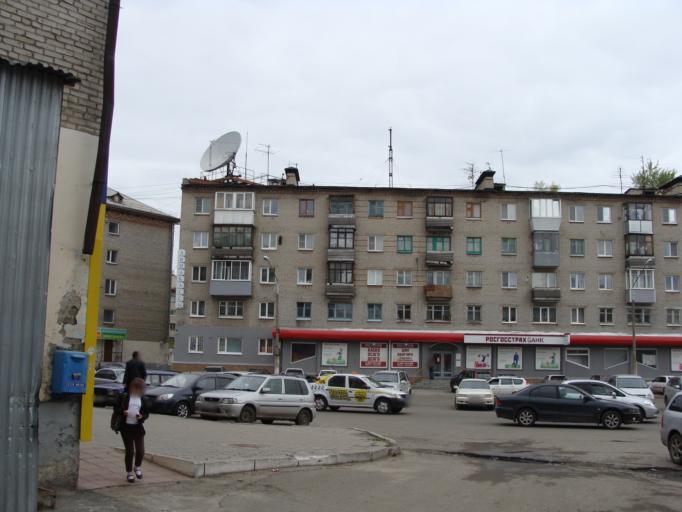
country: RU
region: Altai Krai
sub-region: Gorod Barnaulskiy
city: Barnaul
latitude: 53.3541
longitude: 83.7772
